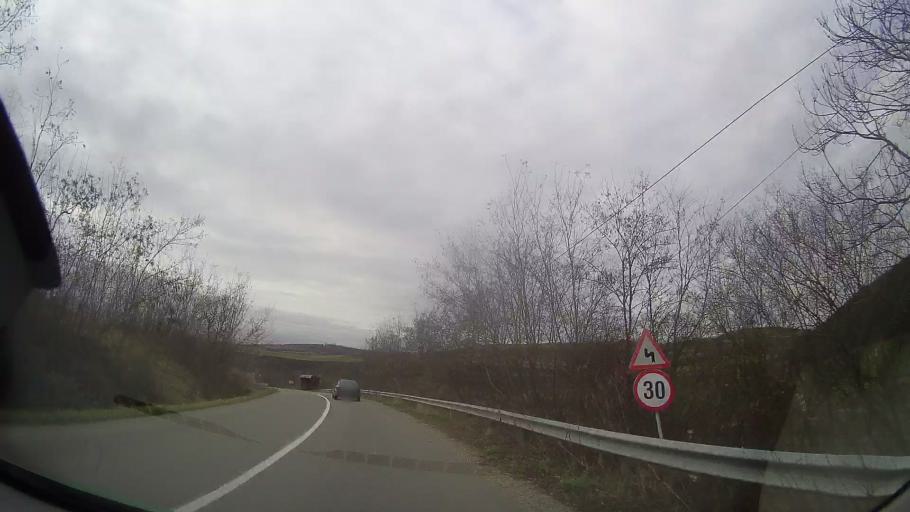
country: RO
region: Bistrita-Nasaud
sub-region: Comuna Milas
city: Milas
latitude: 46.8378
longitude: 24.4394
